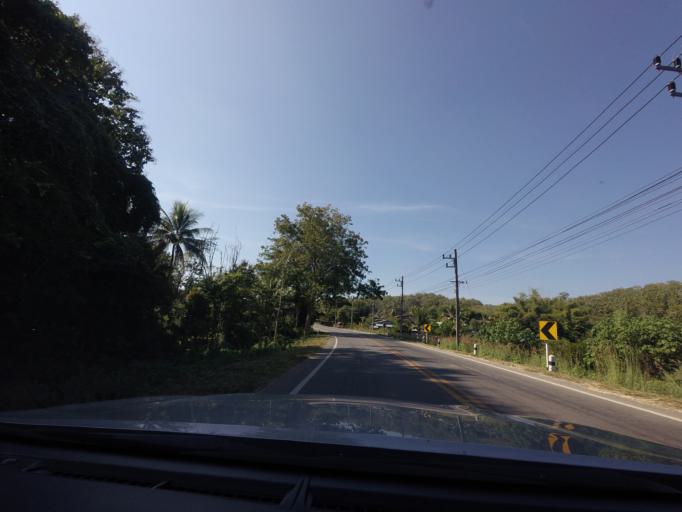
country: TH
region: Sukhothai
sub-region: Amphoe Si Satchanalai
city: Si Satchanalai
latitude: 17.6307
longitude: 99.6979
